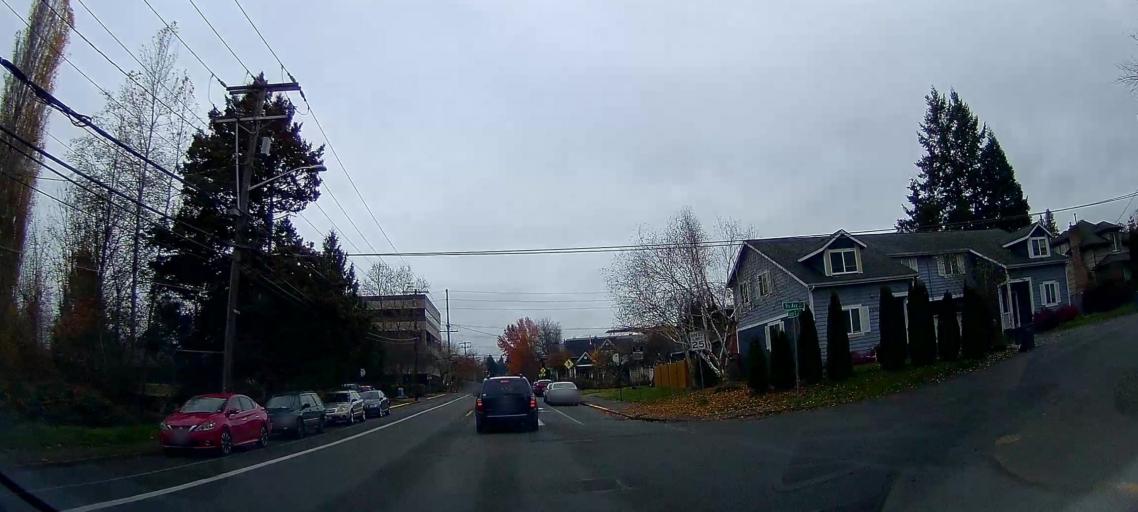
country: US
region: Washington
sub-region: Thurston County
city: Olympia
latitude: 47.0415
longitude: -122.8878
